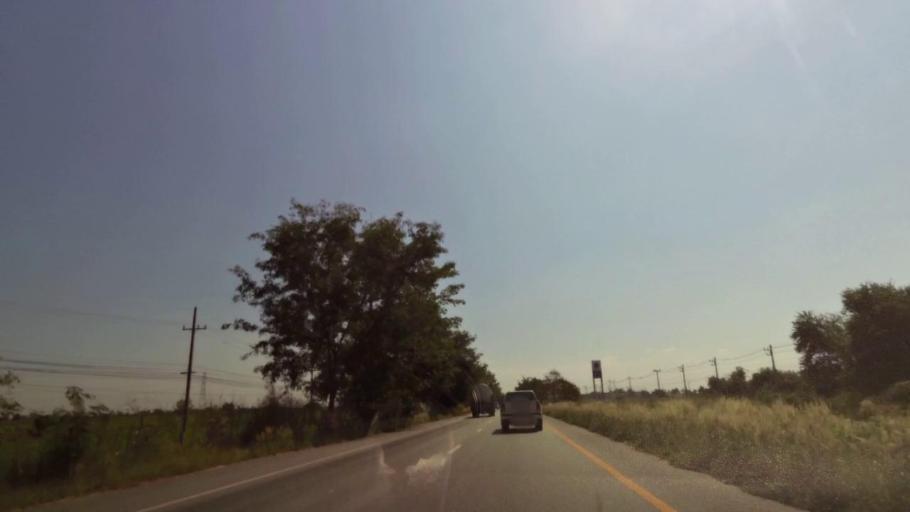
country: TH
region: Nakhon Sawan
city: Kao Liao
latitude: 15.8352
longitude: 100.1178
